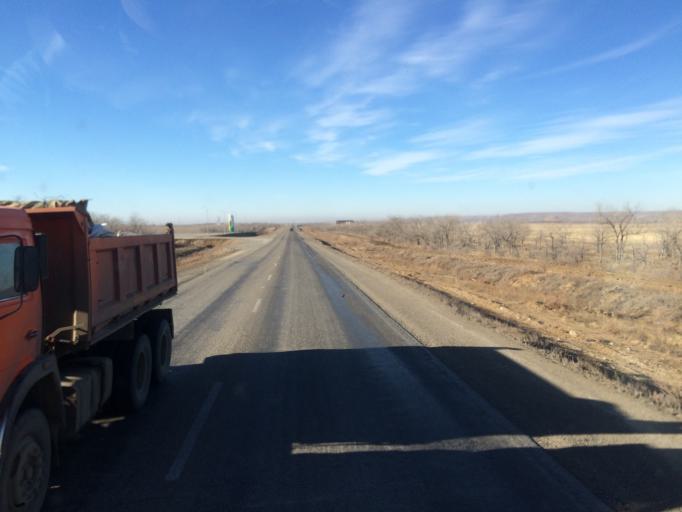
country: KZ
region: Aqtoebe
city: Aqtobe
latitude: 50.2927
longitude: 57.6294
